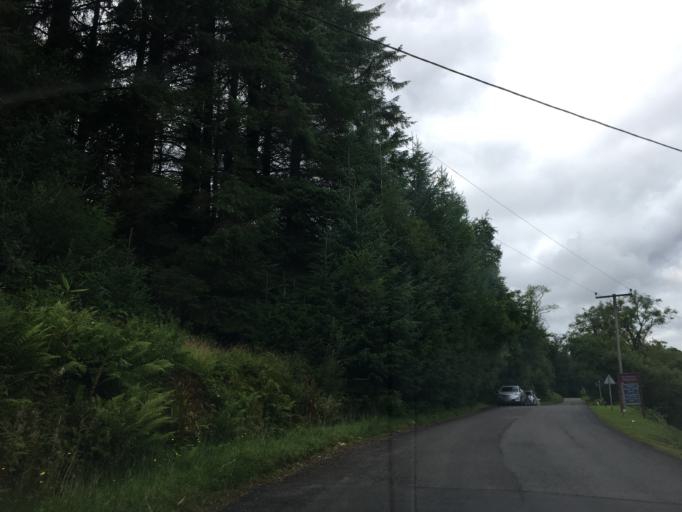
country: GB
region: Scotland
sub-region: Argyll and Bute
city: Oban
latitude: 56.3568
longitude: -5.1775
